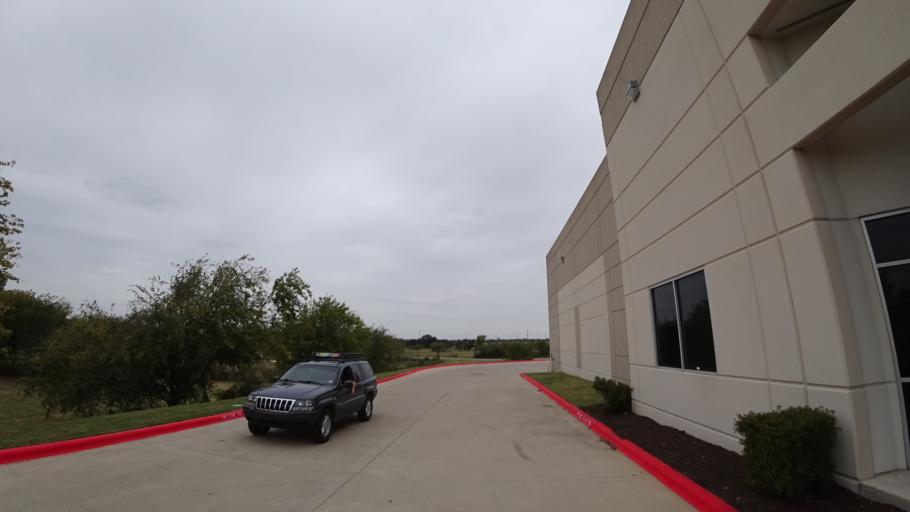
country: US
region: Texas
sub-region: Travis County
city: Wells Branch
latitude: 30.4462
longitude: -97.7100
